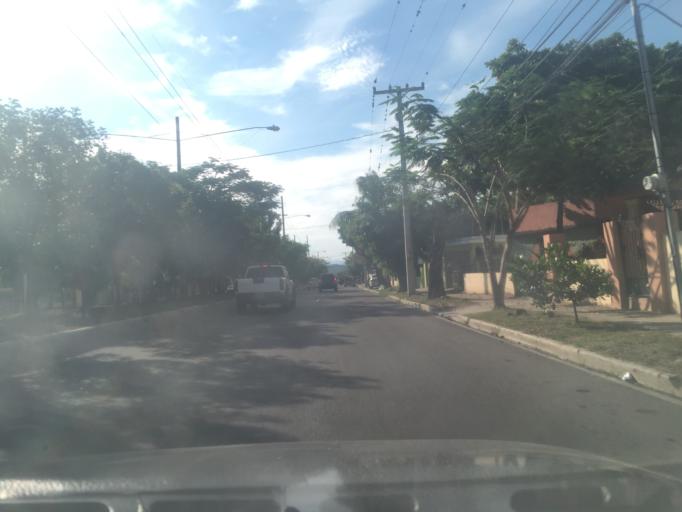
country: DO
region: Santiago
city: Santiago de los Caballeros
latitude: 19.4453
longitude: -70.7408
